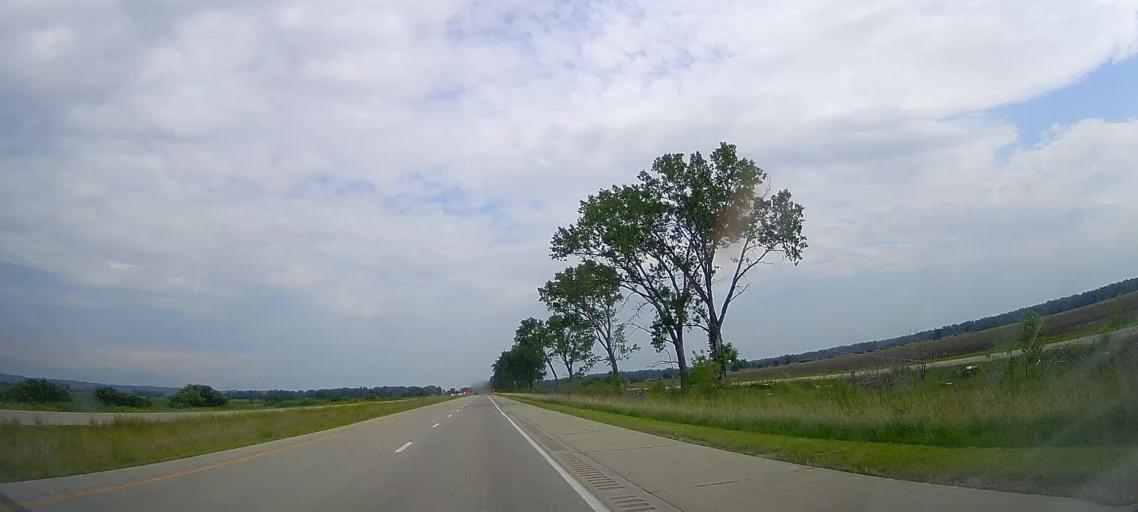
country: US
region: Nebraska
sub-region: Burt County
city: Tekamah
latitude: 41.8332
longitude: -96.0831
